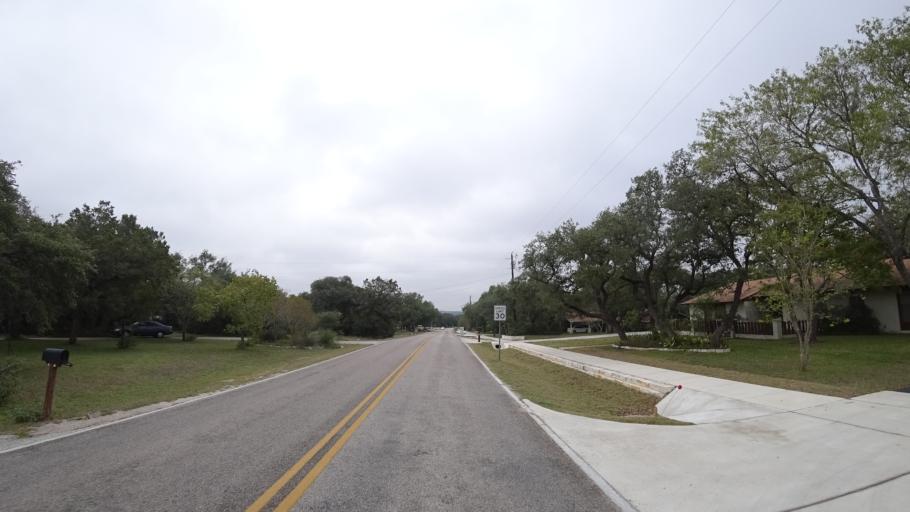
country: US
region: Texas
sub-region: Travis County
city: Barton Creek
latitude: 30.2270
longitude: -97.8977
